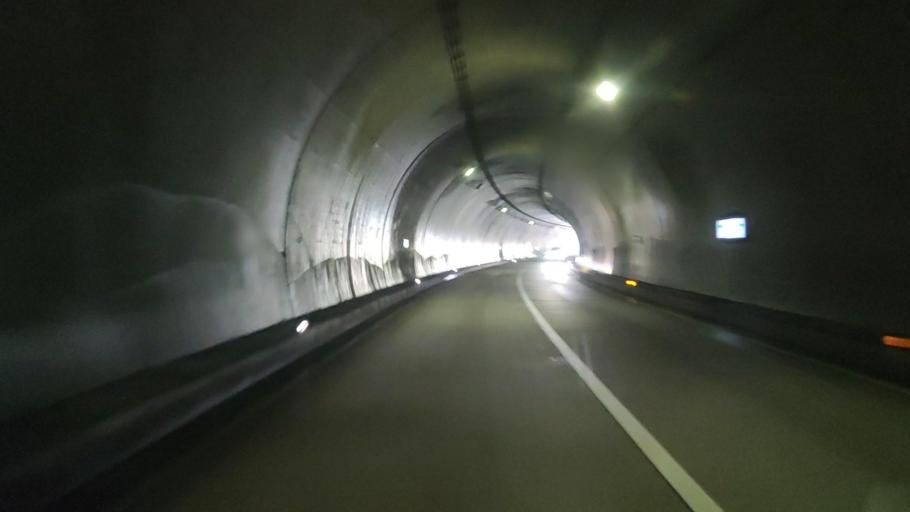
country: JP
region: Wakayama
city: Shingu
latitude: 33.8588
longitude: 135.8519
